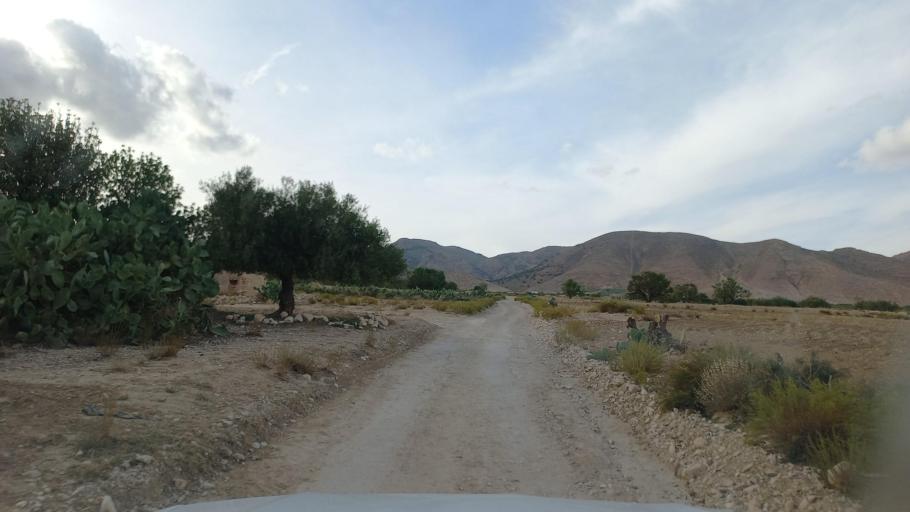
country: TN
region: Al Qasrayn
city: Sbiba
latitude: 35.4435
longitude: 9.0718
